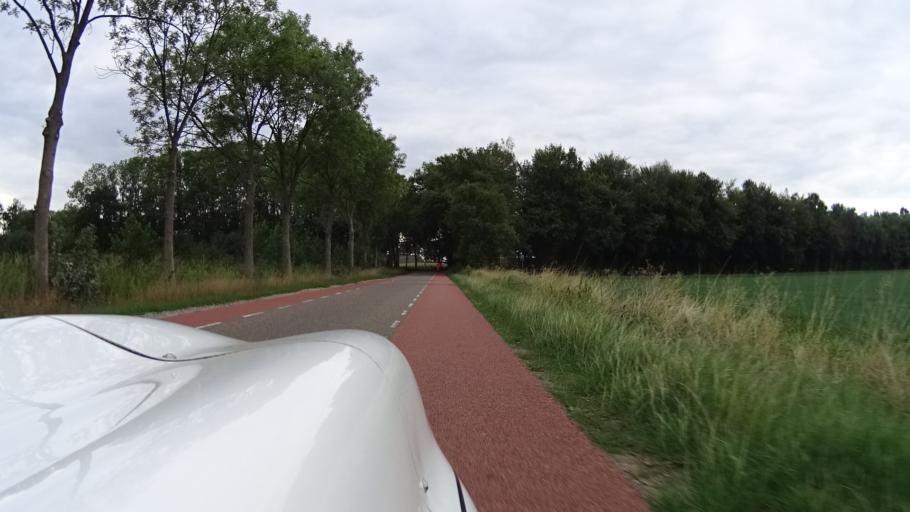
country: NL
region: North Brabant
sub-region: Gemeente Bernheze
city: Loosbroek
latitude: 51.6871
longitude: 5.4944
